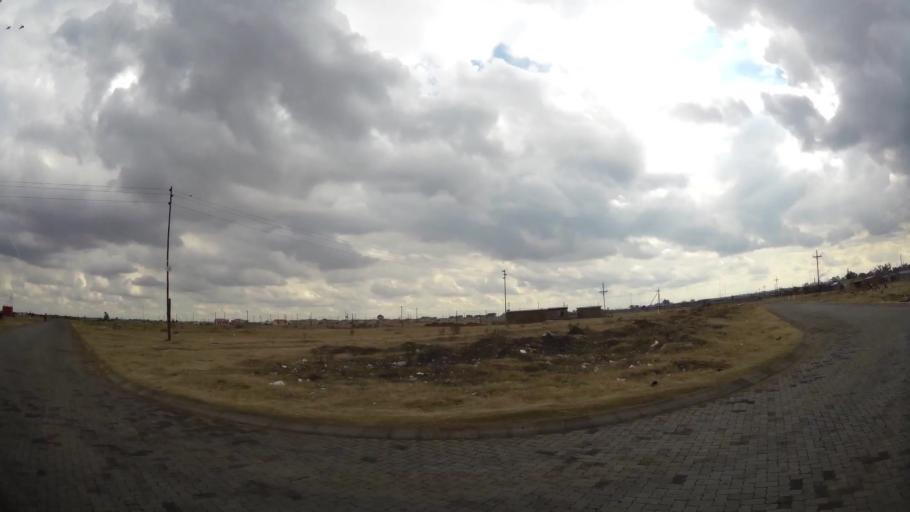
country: ZA
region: Orange Free State
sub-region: Fezile Dabi District Municipality
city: Sasolburg
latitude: -26.8576
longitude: 27.8733
